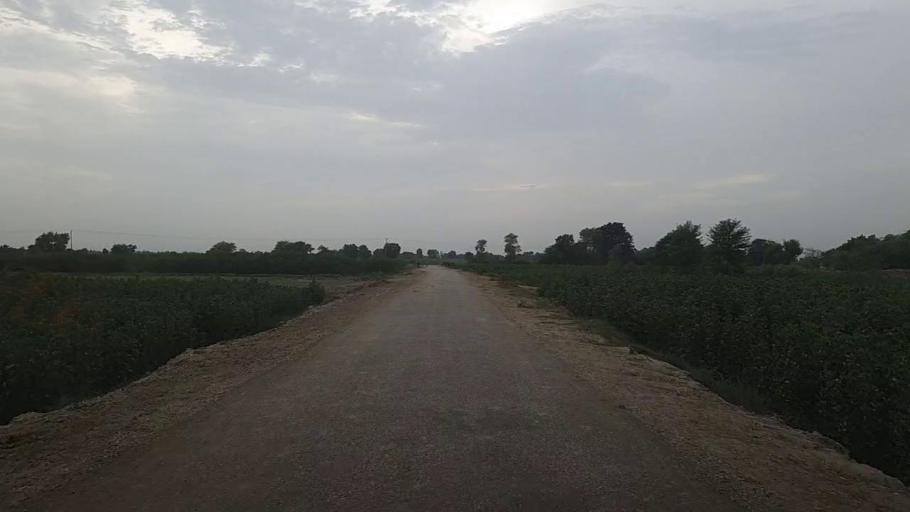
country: PK
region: Sindh
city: Karaundi
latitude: 26.9572
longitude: 68.3595
